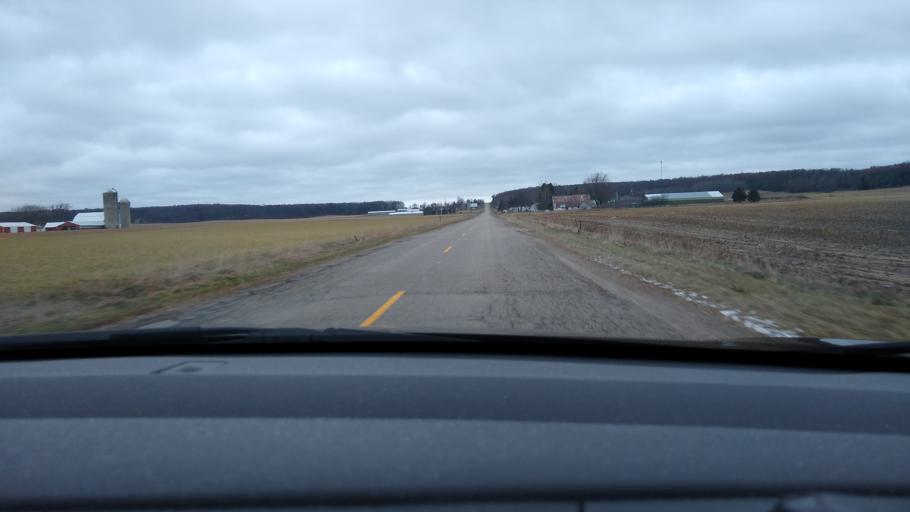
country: US
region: Michigan
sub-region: Missaukee County
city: Lake City
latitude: 44.2750
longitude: -85.0540
